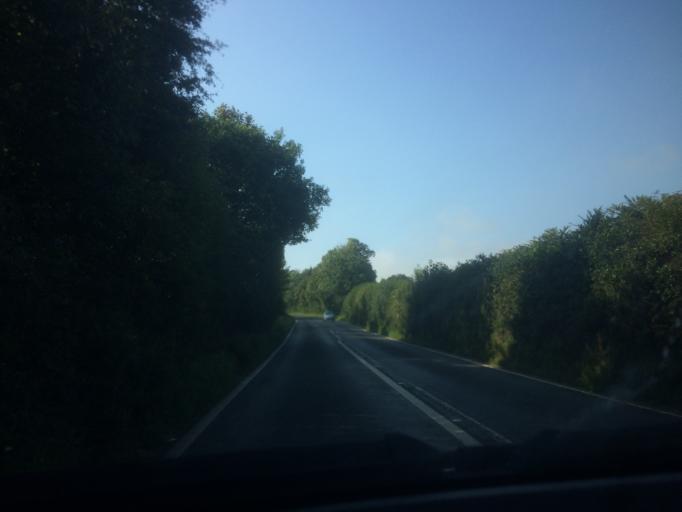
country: GB
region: England
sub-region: Cornwall
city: Pillaton
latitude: 50.4420
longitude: -4.2565
